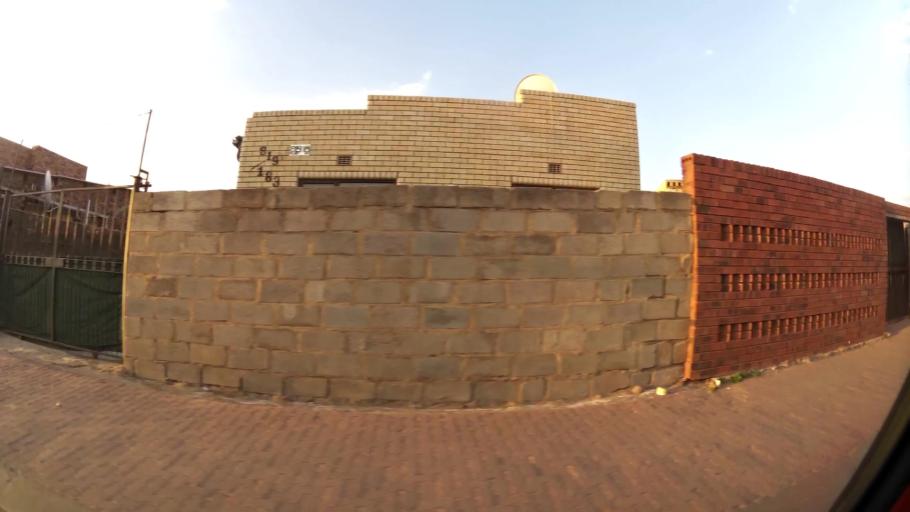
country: ZA
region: Gauteng
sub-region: City of Johannesburg Metropolitan Municipality
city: Soweto
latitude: -26.2340
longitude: 27.8994
